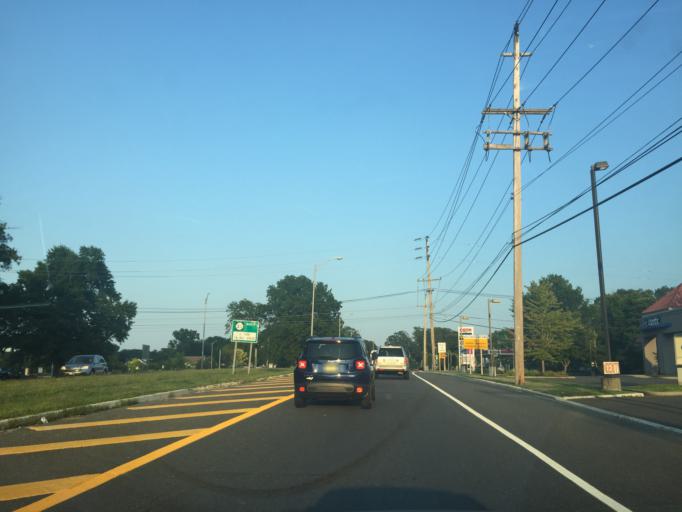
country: US
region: New Jersey
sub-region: Monmouth County
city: Wanamassa
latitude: 40.2265
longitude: -74.0407
